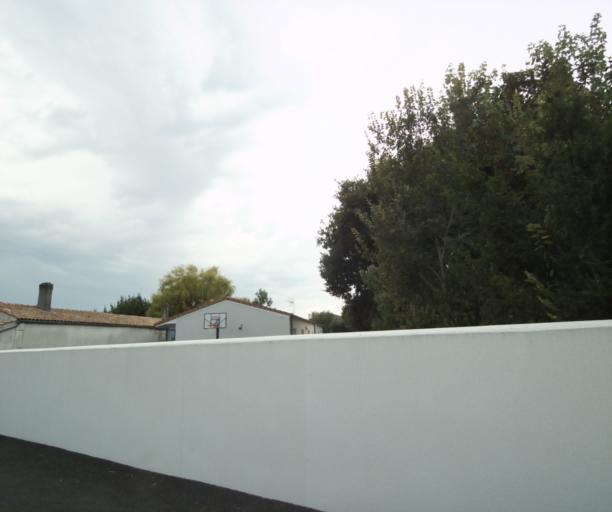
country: FR
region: Poitou-Charentes
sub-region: Departement de la Charente-Maritime
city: Tonnay-Charente
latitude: 45.9473
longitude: -0.9005
